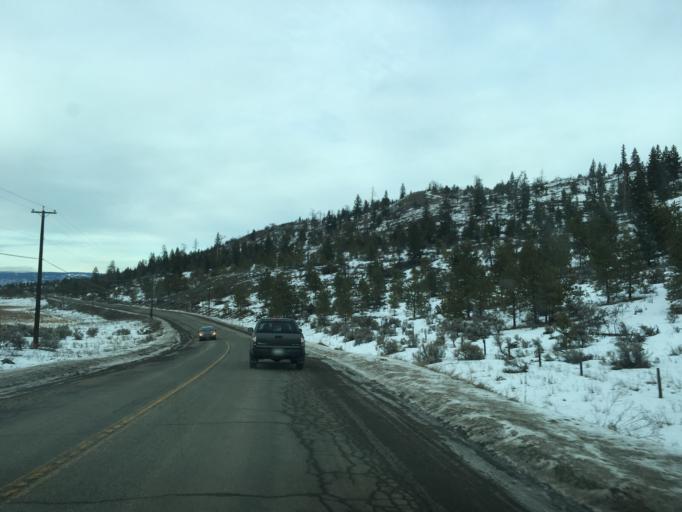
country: CA
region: British Columbia
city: Kamloops
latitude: 50.6408
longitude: -120.4493
